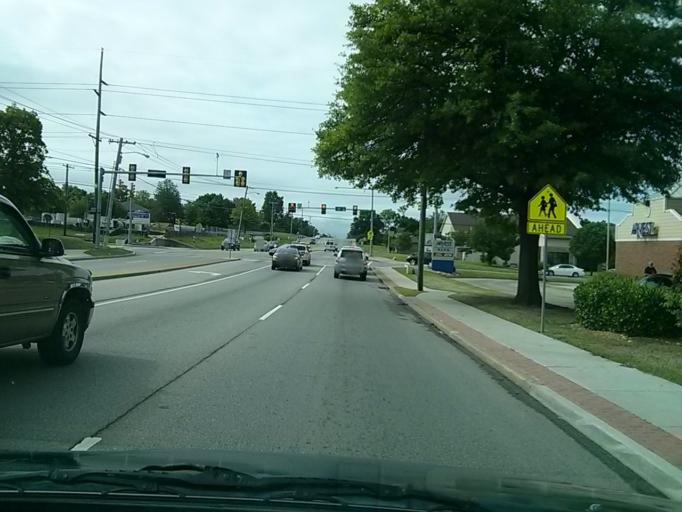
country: US
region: Oklahoma
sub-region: Tulsa County
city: Tulsa
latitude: 36.1122
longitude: -95.9225
